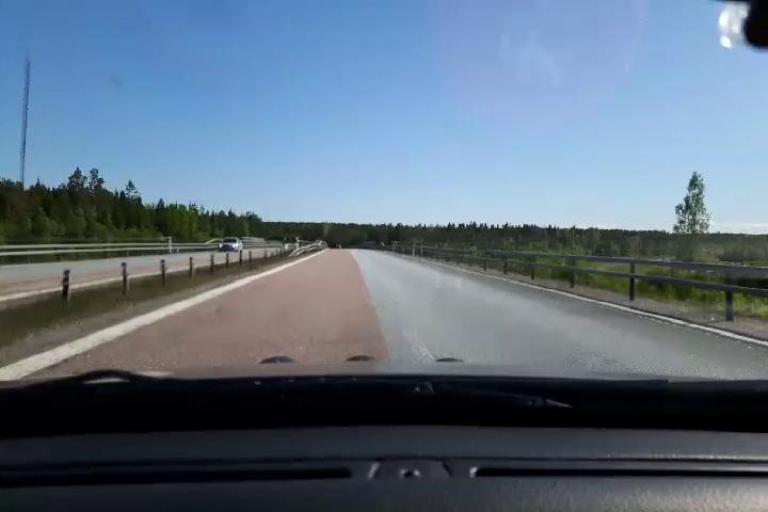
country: SE
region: Gaevleborg
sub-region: Soderhamns Kommun
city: Soderhamn
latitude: 61.3358
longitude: 17.0172
